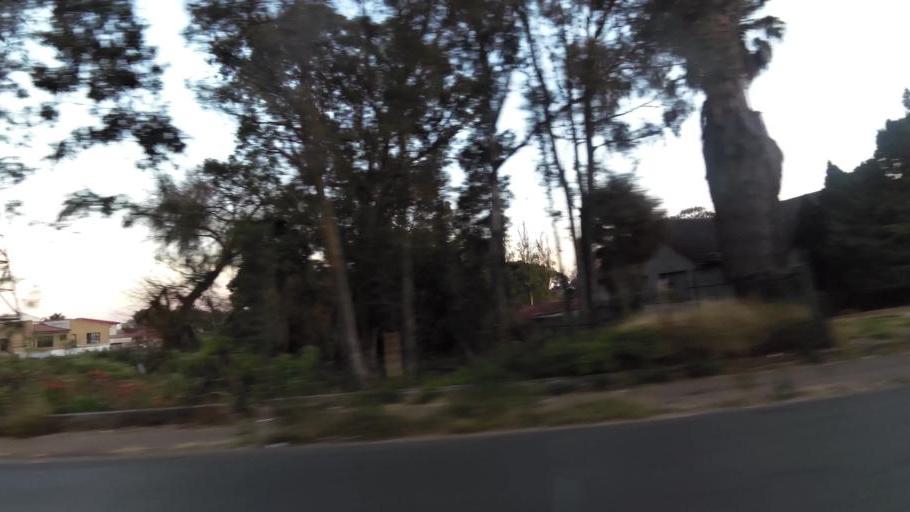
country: ZA
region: Gauteng
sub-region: City of Johannesburg Metropolitan Municipality
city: Johannesburg
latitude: -26.2018
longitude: 28.0006
